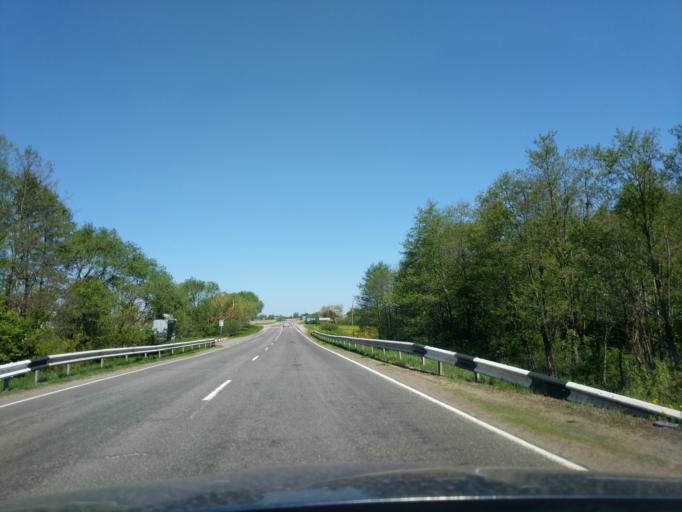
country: BY
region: Minsk
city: Il'ya
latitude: 54.2975
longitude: 27.4799
